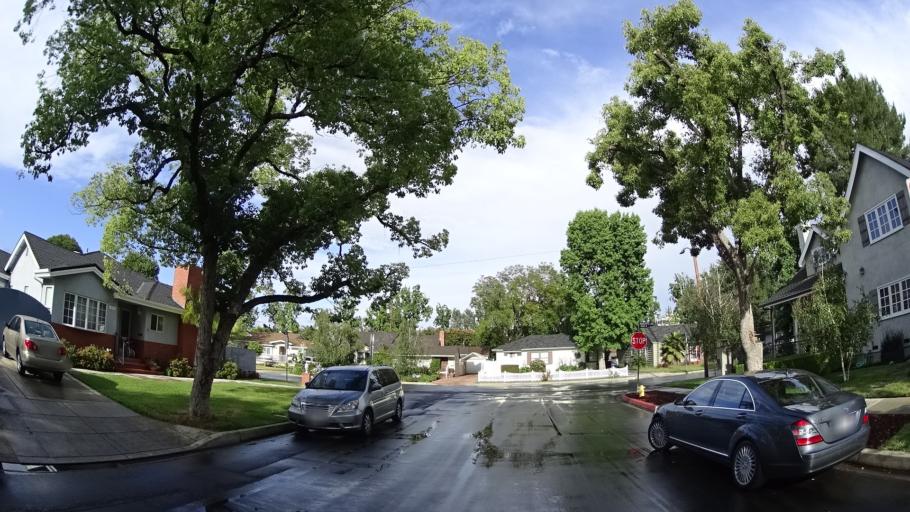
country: US
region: California
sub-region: Los Angeles County
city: Sherman Oaks
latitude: 34.1592
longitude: -118.4357
